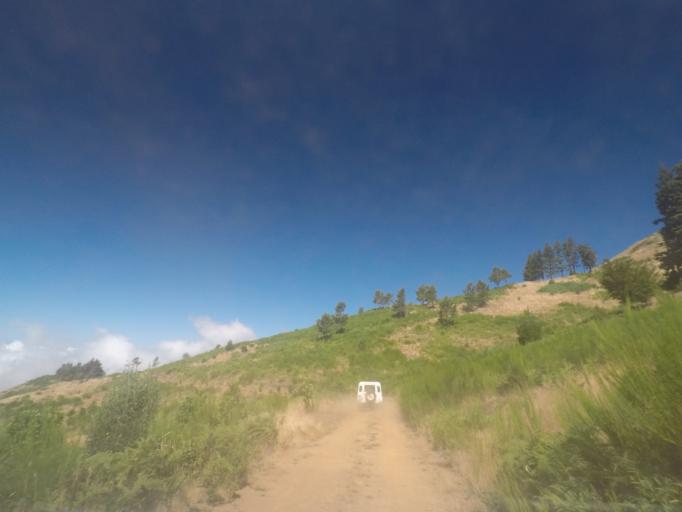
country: PT
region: Madeira
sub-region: Funchal
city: Nossa Senhora do Monte
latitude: 32.7064
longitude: -16.9108
